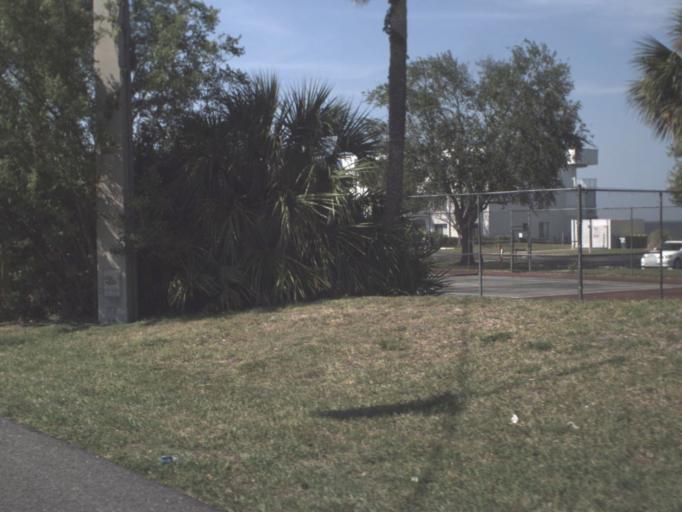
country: US
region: Florida
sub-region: Brevard County
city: Port Saint John
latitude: 28.4780
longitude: -80.7690
